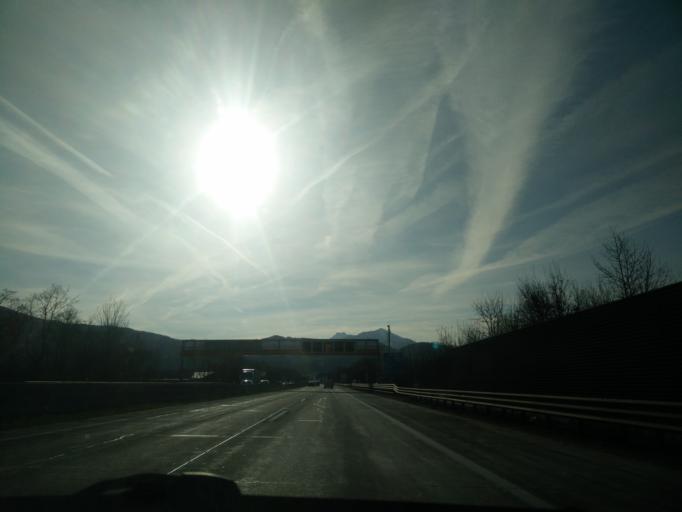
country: AT
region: Salzburg
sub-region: Politischer Bezirk Salzburg-Umgebung
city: Anif
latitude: 47.7369
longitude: 13.0629
